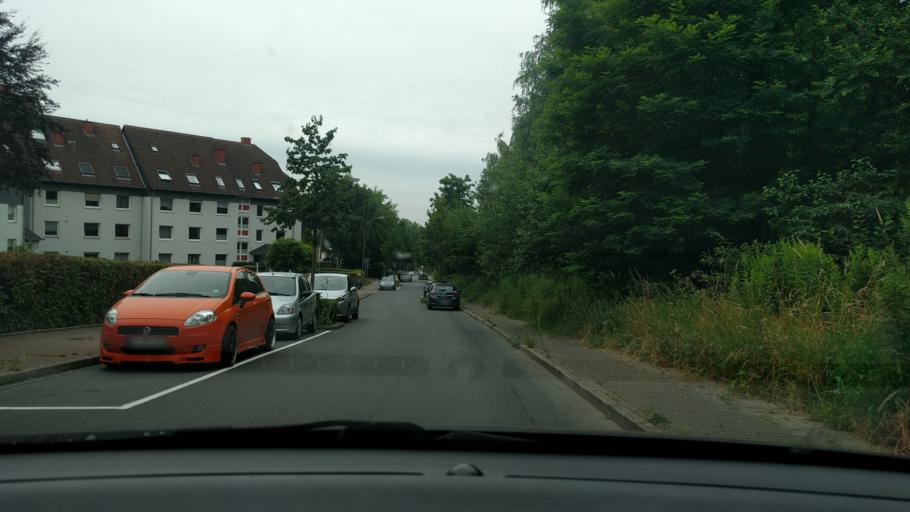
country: DE
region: North Rhine-Westphalia
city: Witten
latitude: 51.4713
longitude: 7.3308
